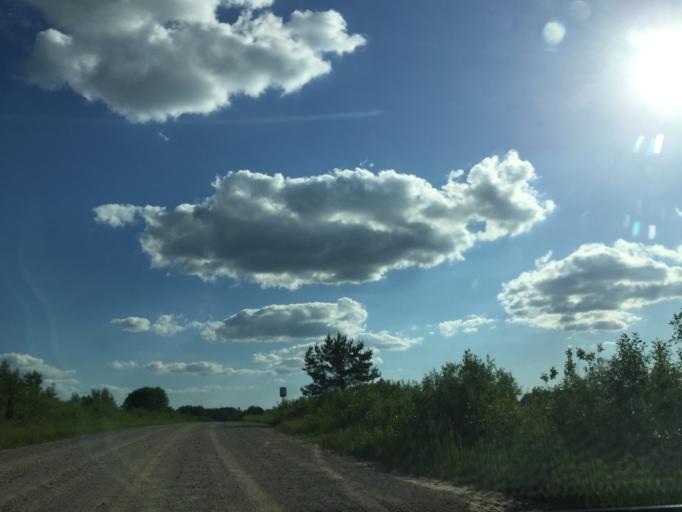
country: LV
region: Kandava
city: Kandava
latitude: 56.8890
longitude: 22.7845
